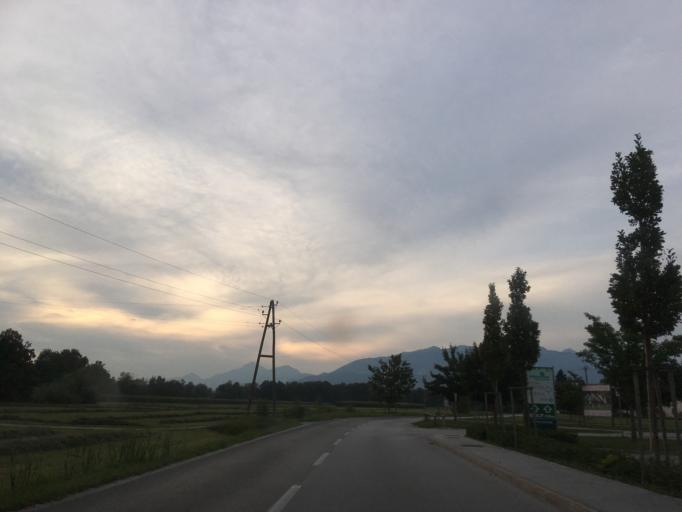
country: SI
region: Kamnik
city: Smarca
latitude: 46.1858
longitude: 14.6053
